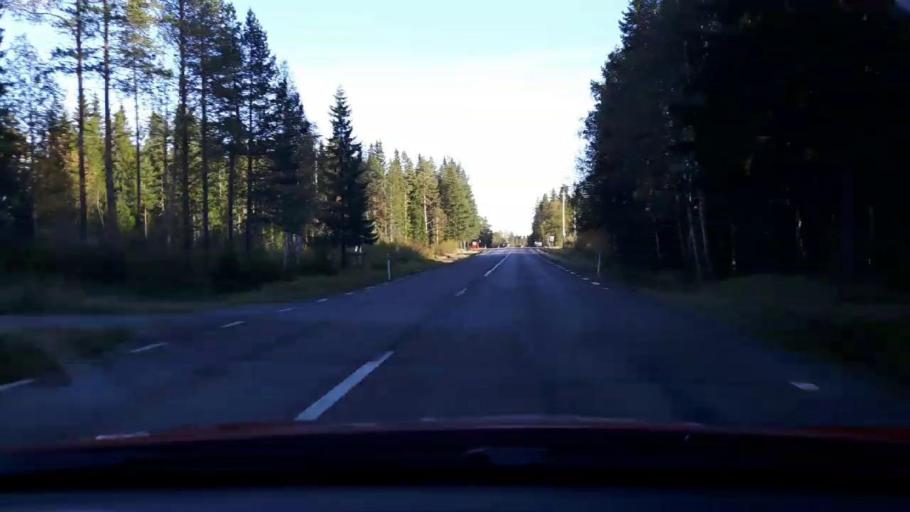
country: SE
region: Jaemtland
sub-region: OEstersunds Kommun
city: Brunflo
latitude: 63.0262
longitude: 14.9160
